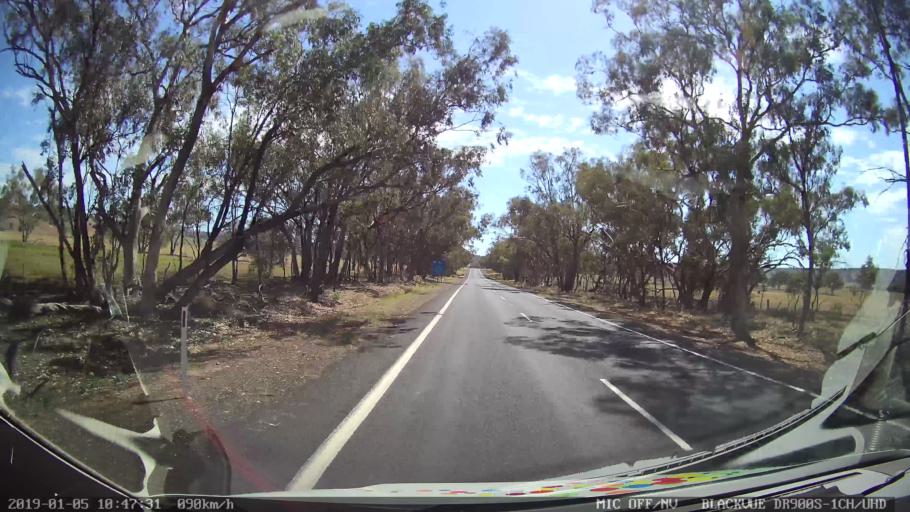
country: AU
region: New South Wales
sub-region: Warrumbungle Shire
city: Coonabarabran
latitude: -31.4443
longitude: 149.0340
